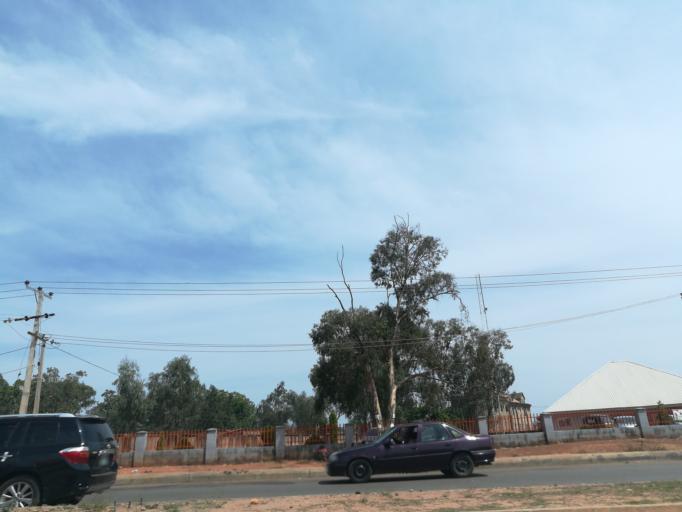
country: NG
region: Plateau
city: Bukuru
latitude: 9.8503
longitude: 8.8673
